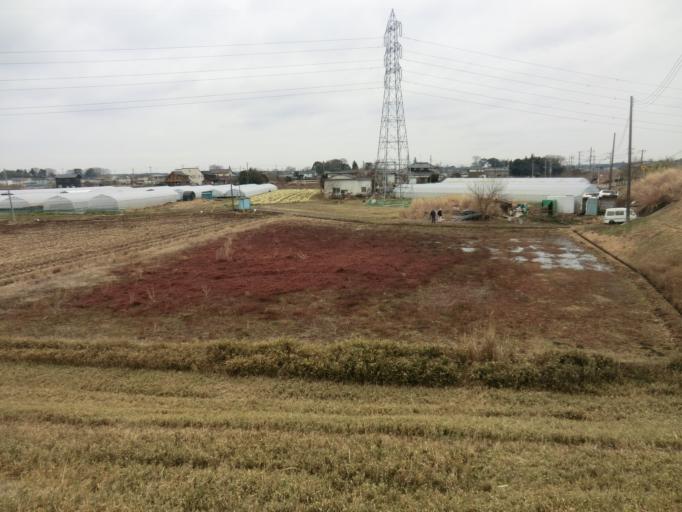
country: JP
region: Ibaraki
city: Naka
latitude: 36.1123
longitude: 140.1441
